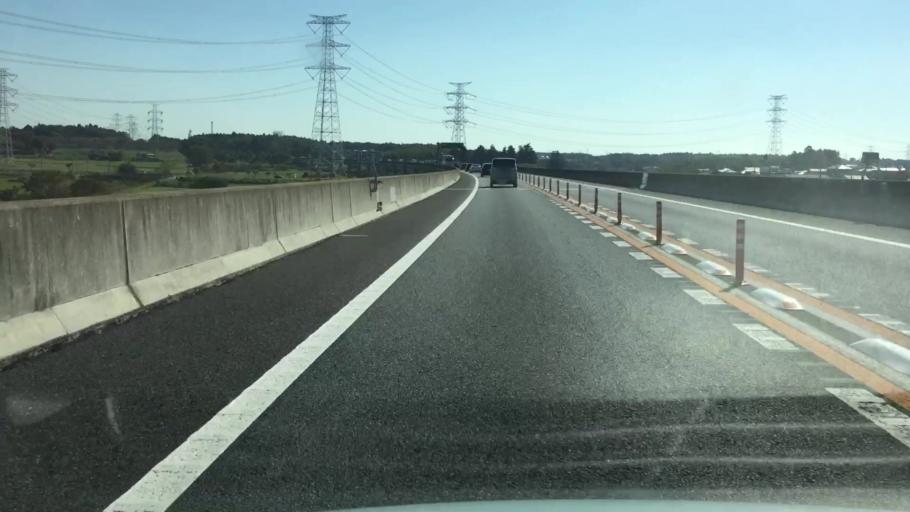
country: JP
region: Ibaraki
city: Ushiku
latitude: 35.9955
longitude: 140.1551
